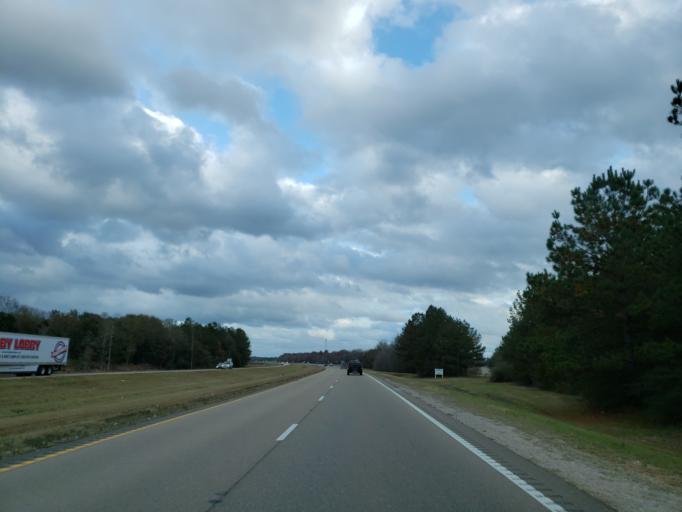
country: US
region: Mississippi
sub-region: Perry County
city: New Augusta
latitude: 31.1221
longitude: -88.8429
